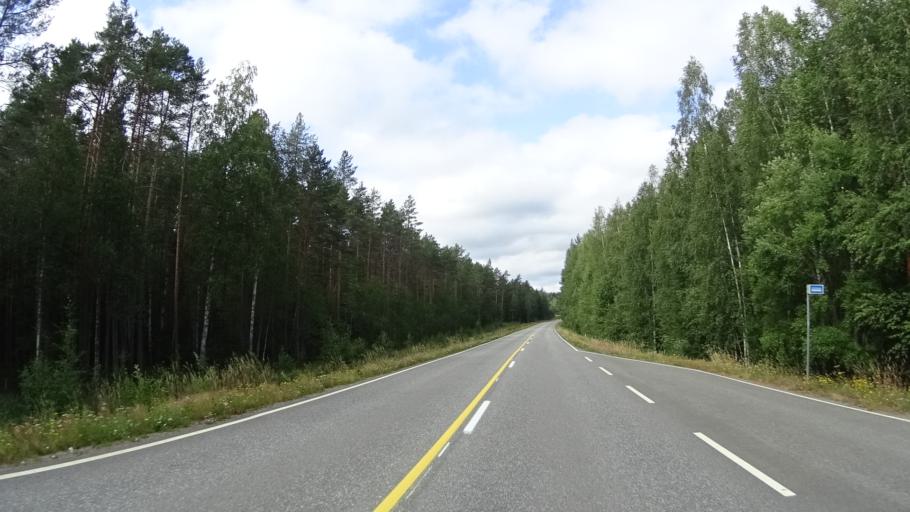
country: FI
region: Pirkanmaa
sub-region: Tampere
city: Luopioinen
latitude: 61.4968
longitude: 24.8022
